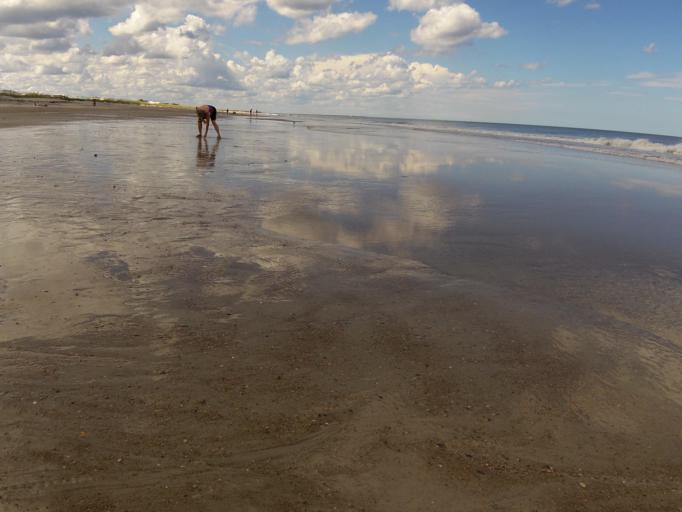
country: US
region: Florida
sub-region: Nassau County
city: Fernandina Beach
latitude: 30.6830
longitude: -81.4274
